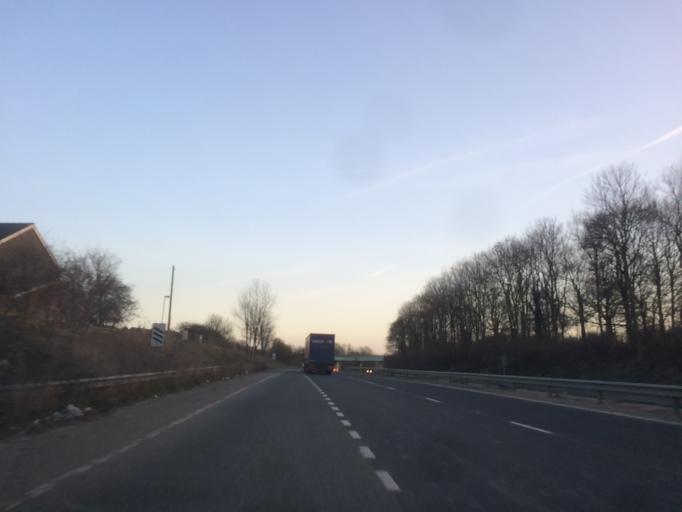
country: GB
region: England
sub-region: City and Borough of Wakefield
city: Ferrybridge
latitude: 53.7105
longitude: -1.2694
